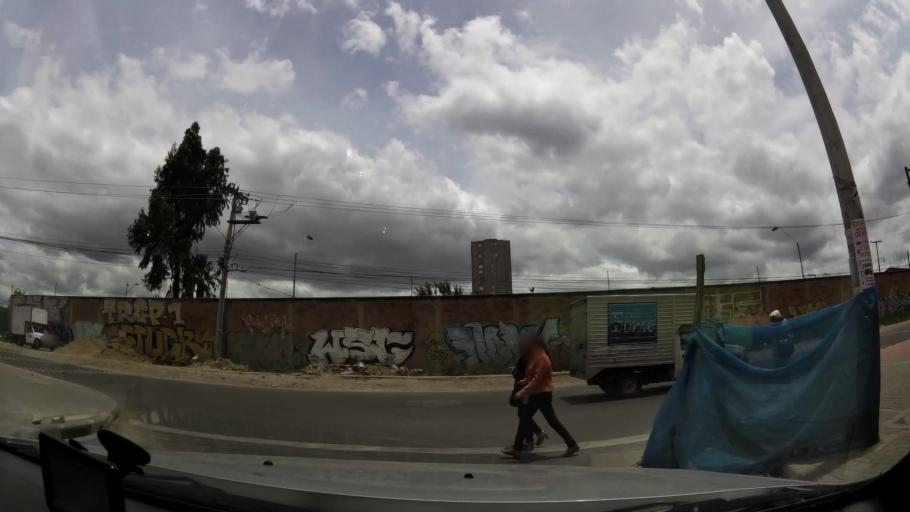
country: CO
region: Bogota D.C.
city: Bogota
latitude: 4.6479
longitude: -74.1460
